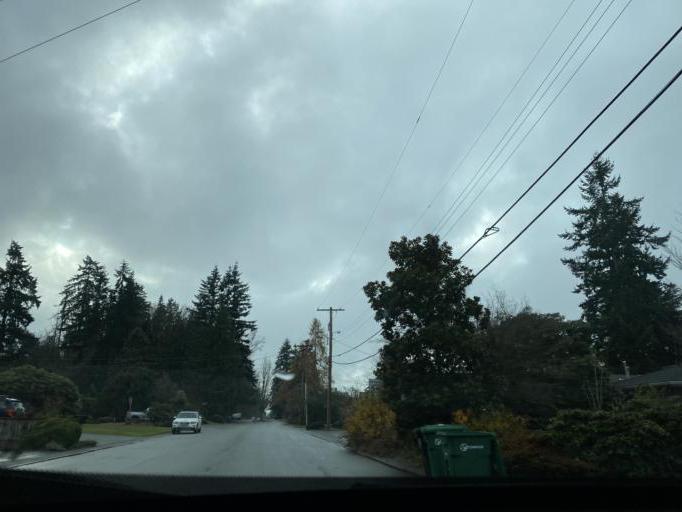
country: US
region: Washington
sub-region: King County
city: Mercer Island
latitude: 47.5468
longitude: -122.2270
